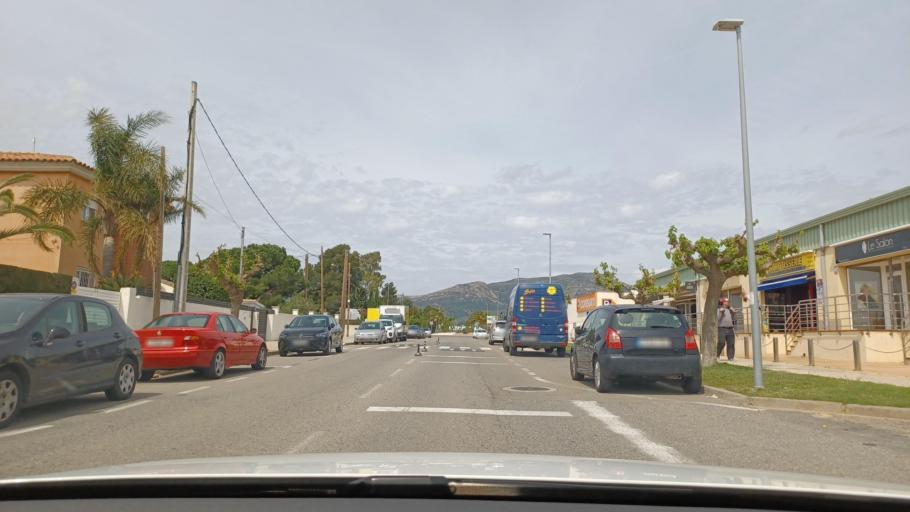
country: ES
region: Catalonia
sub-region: Provincia de Tarragona
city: Colldejou
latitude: 41.0182
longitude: 0.9412
